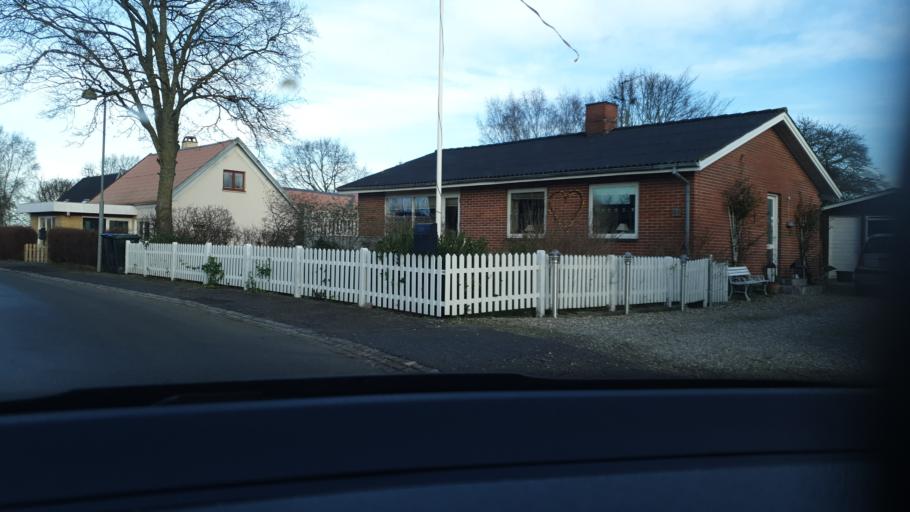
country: DK
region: Zealand
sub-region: Odsherred Kommune
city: Hojby
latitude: 55.9123
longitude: 11.6096
